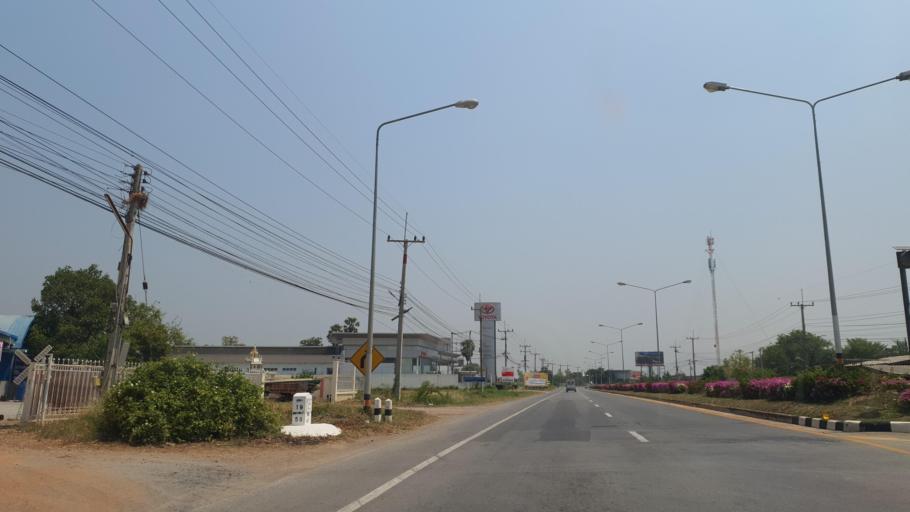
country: TH
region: Kanchanaburi
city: Phanom Thuan
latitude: 14.2405
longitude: 99.8068
